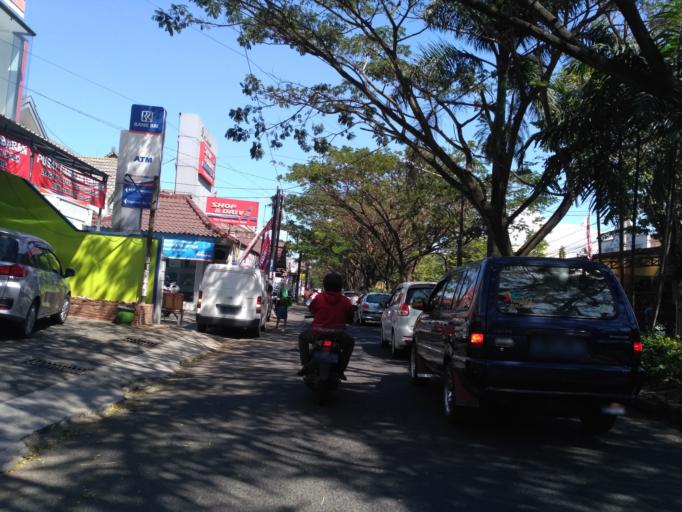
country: ID
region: East Java
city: Malang
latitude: -7.9793
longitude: 112.6594
